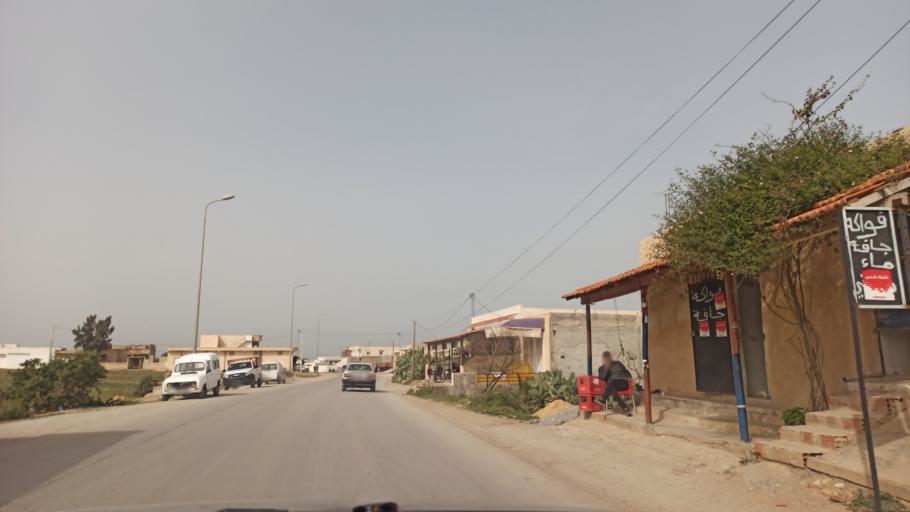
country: TN
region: Zaghwan
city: Zaghouan
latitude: 36.4165
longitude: 10.1233
